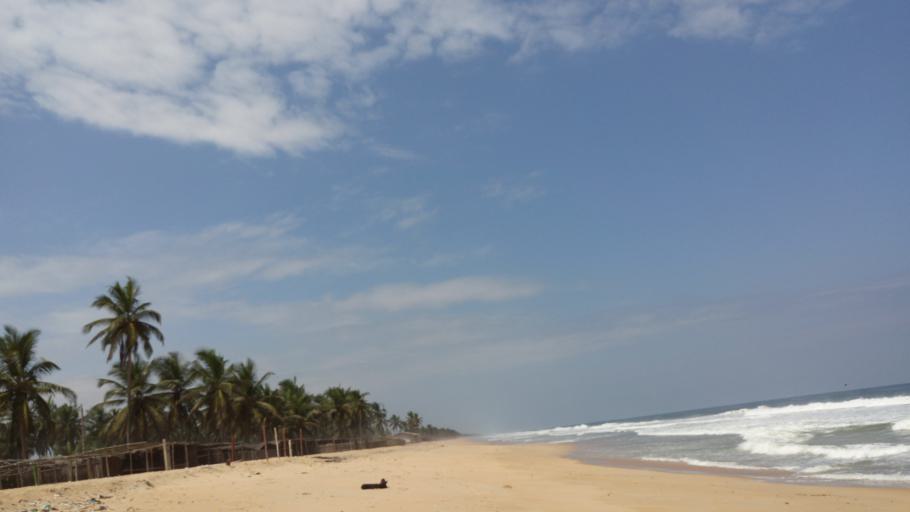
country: CI
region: Sud-Comoe
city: Grand-Bassam
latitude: 5.1870
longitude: -3.6906
